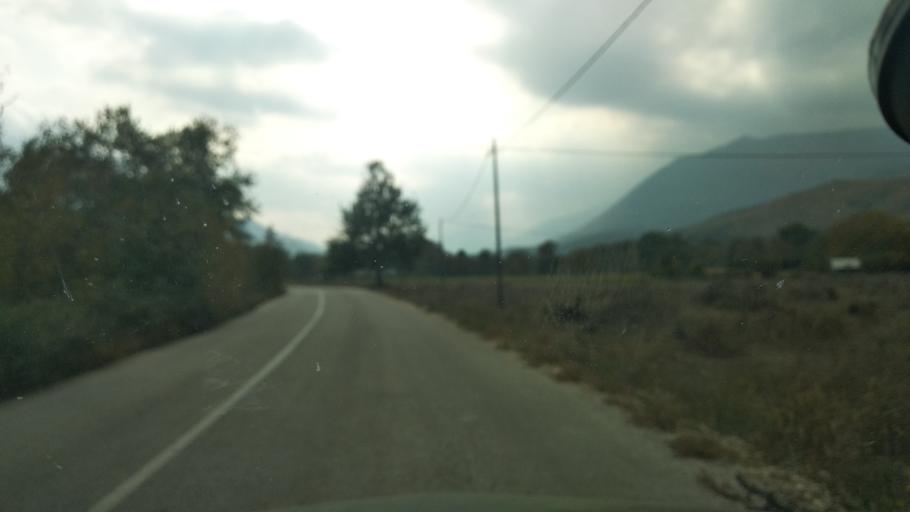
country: GR
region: Thessaly
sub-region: Trikala
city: Kastraki
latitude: 39.7199
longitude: 21.5264
